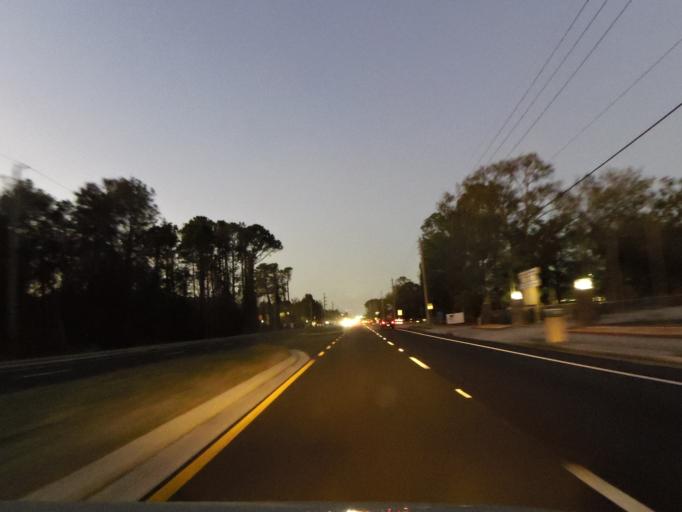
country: US
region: Florida
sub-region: Clay County
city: Lakeside
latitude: 30.1216
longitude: -81.7763
